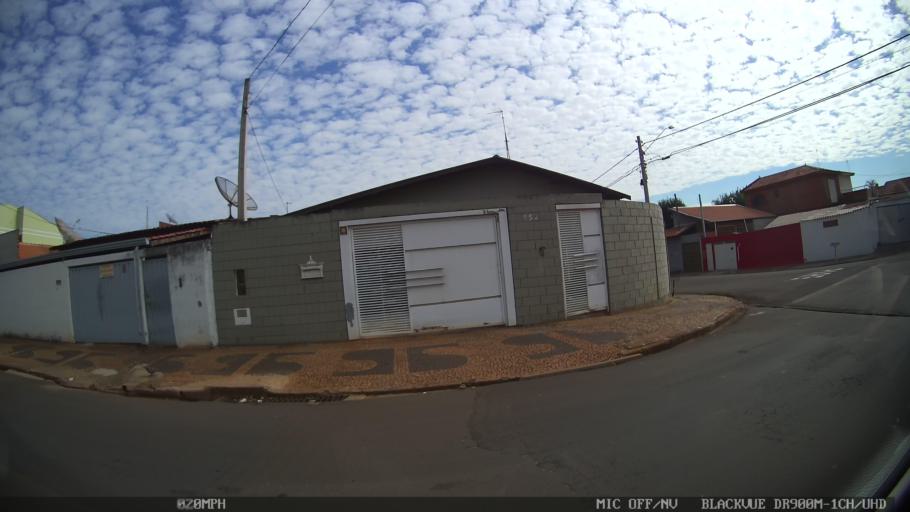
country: BR
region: Sao Paulo
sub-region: Santa Barbara D'Oeste
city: Santa Barbara d'Oeste
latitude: -22.7635
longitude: -47.4054
